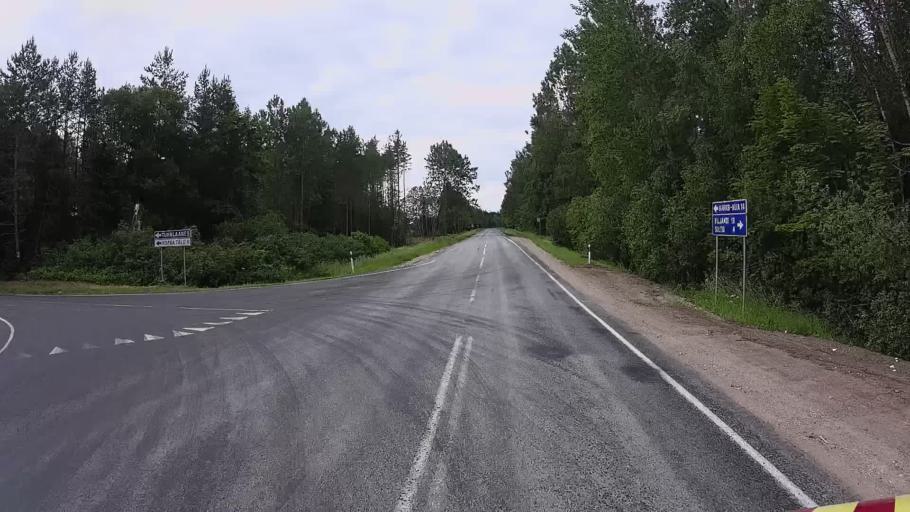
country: EE
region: Viljandimaa
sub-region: Karksi vald
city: Karksi-Nuia
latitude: 58.2094
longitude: 25.6213
